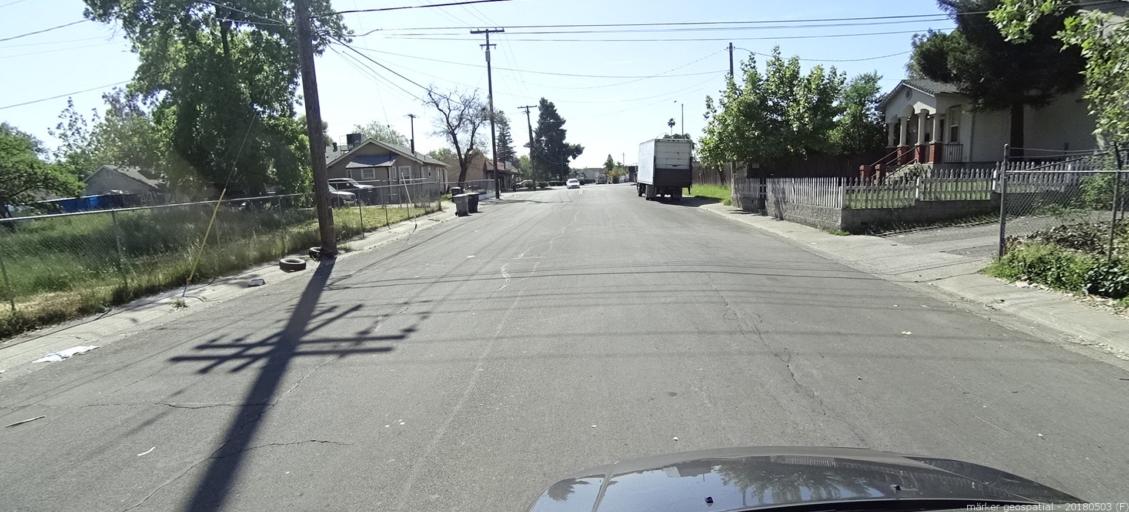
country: US
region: California
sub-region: Sacramento County
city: Arden-Arcade
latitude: 38.6199
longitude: -121.4389
